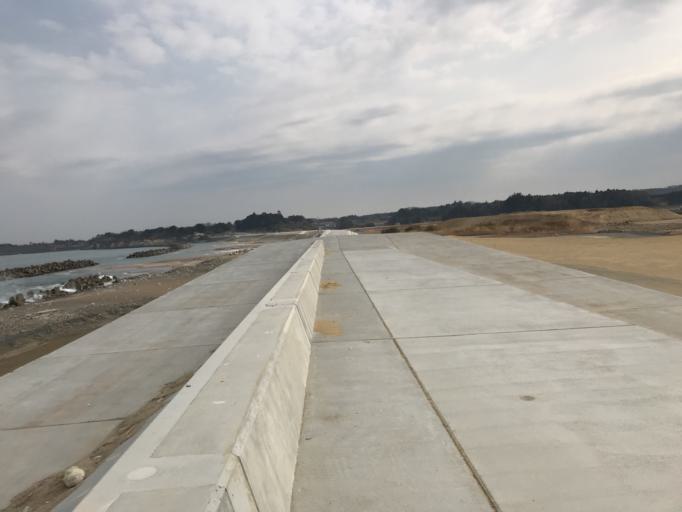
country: JP
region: Miyagi
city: Marumori
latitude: 37.7739
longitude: 140.9884
